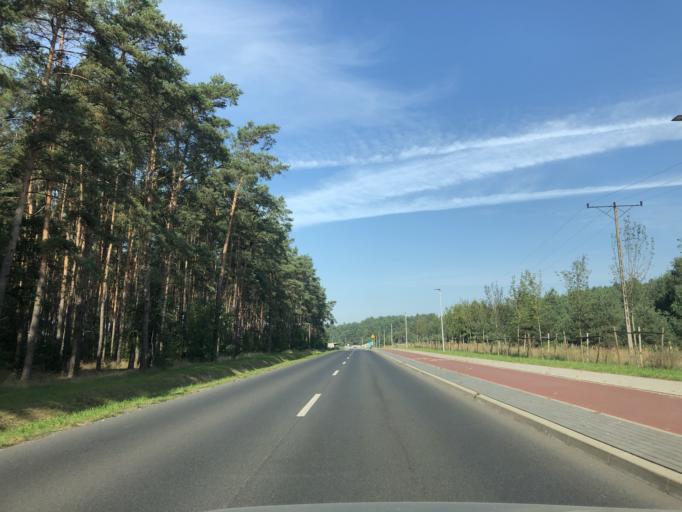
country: PL
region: Greater Poland Voivodeship
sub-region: Powiat pilski
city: Pila
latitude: 53.1375
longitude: 16.7921
